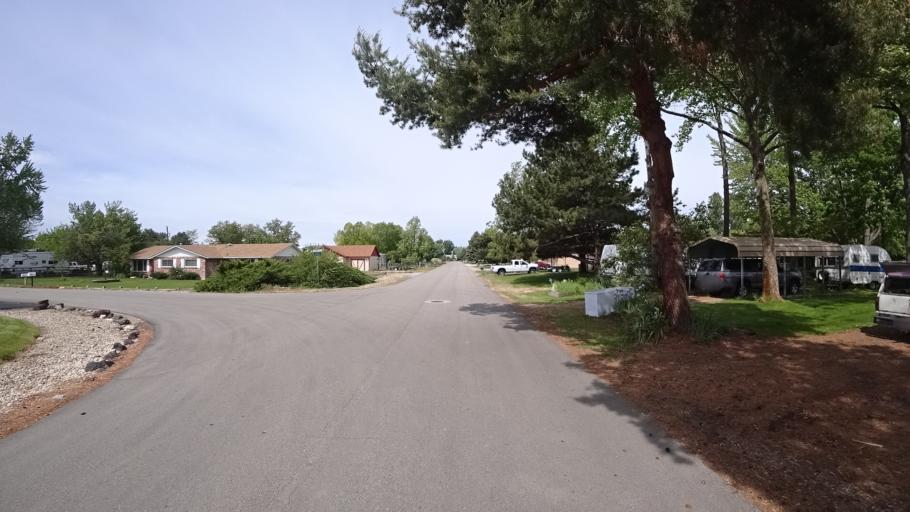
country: US
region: Idaho
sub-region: Ada County
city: Meridian
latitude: 43.5822
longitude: -116.3187
